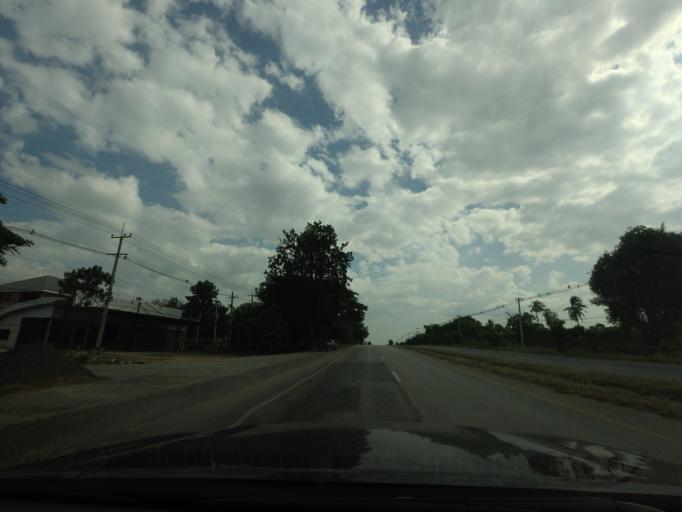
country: TH
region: Lop Buri
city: Chai Badan
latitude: 15.2467
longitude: 101.1258
